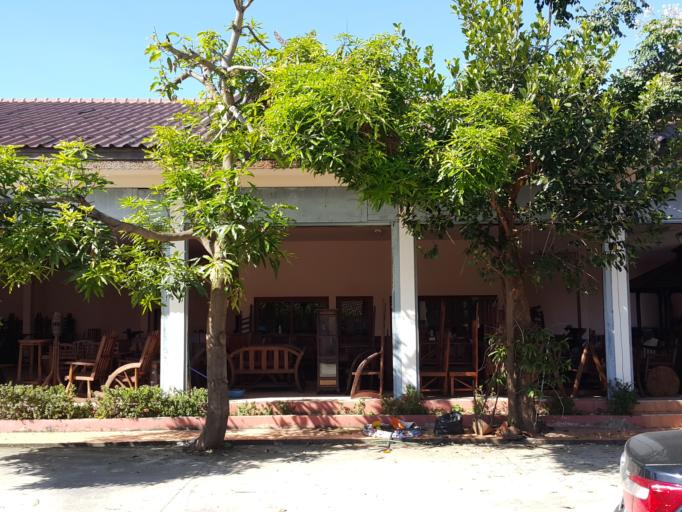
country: TH
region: Chiang Mai
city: Hang Dong
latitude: 18.6886
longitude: 98.9471
